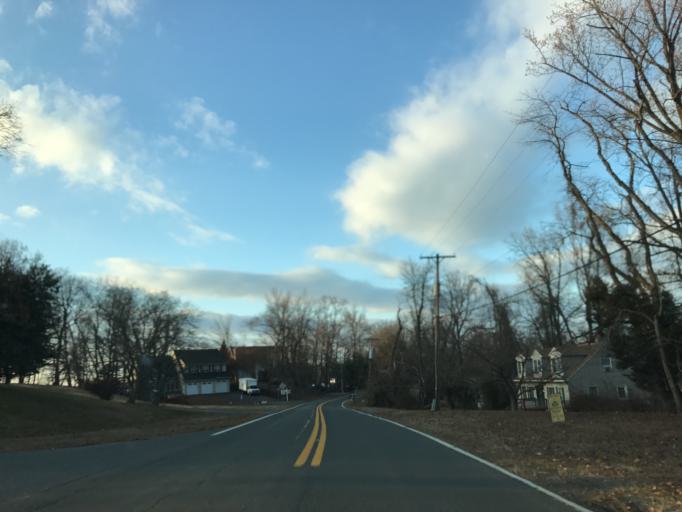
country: US
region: Maryland
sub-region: Cecil County
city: Charlestown
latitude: 39.4650
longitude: -75.9954
